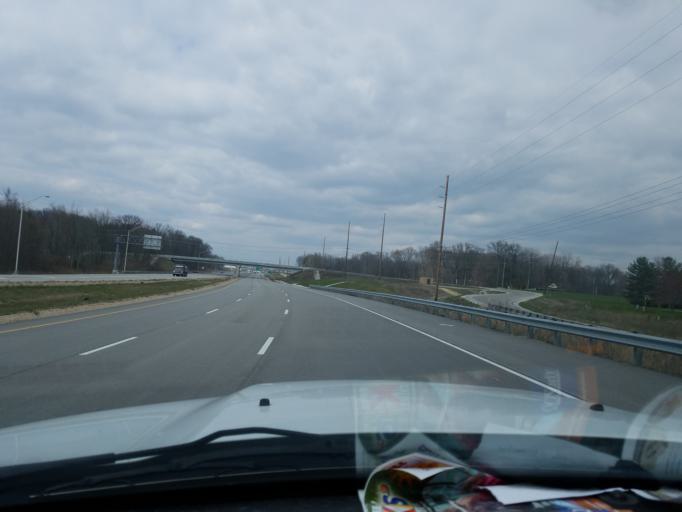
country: US
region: Indiana
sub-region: Vigo County
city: Terre Haute
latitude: 39.4167
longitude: -87.3328
